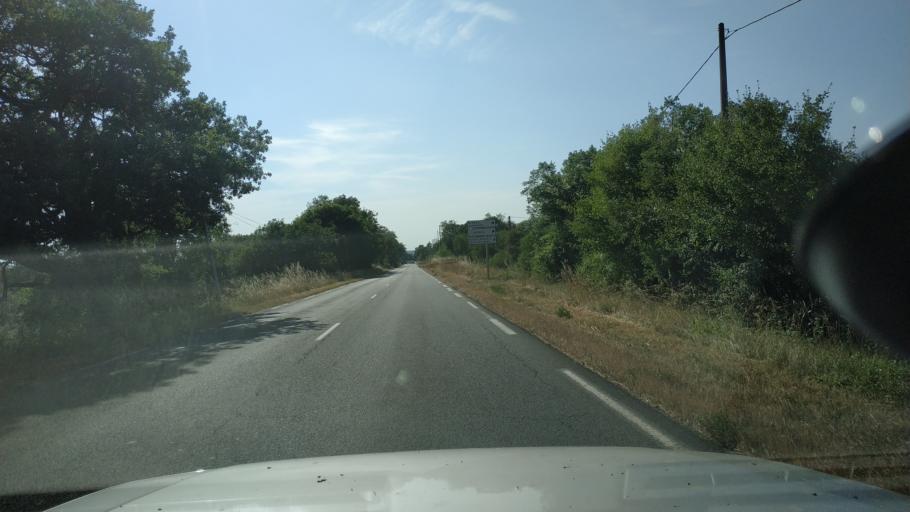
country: FR
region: Midi-Pyrenees
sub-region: Departement du Lot
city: Gramat
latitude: 44.7937
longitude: 1.6970
